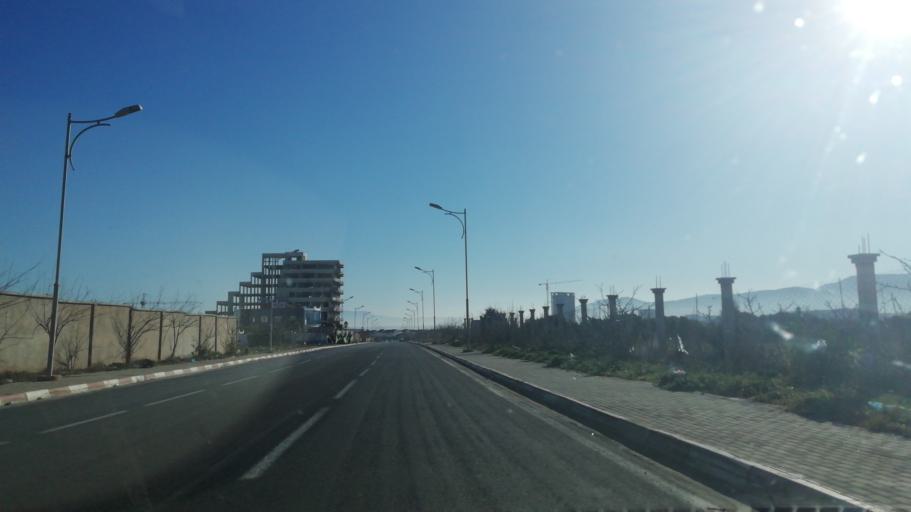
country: DZ
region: Oran
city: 'Ain el Turk
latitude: 35.7581
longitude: -0.7971
